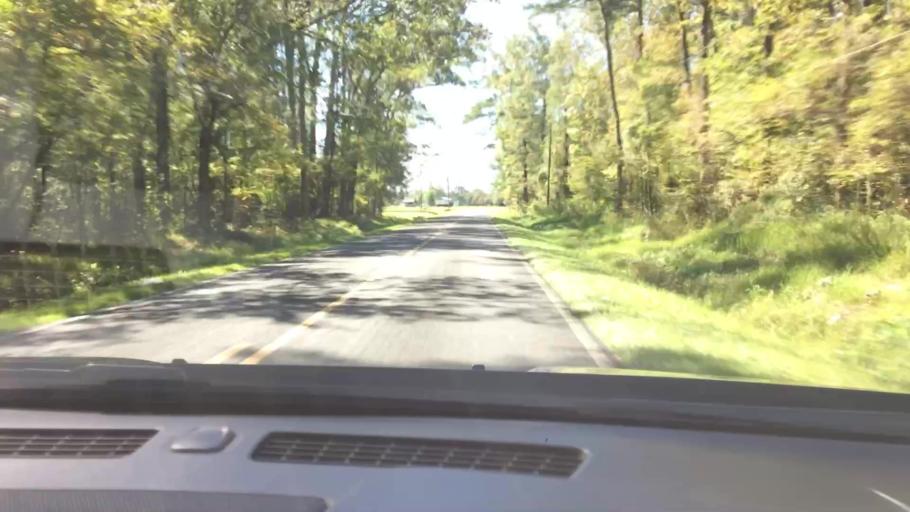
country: US
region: North Carolina
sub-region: Pitt County
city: Grifton
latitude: 35.3008
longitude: -77.3207
